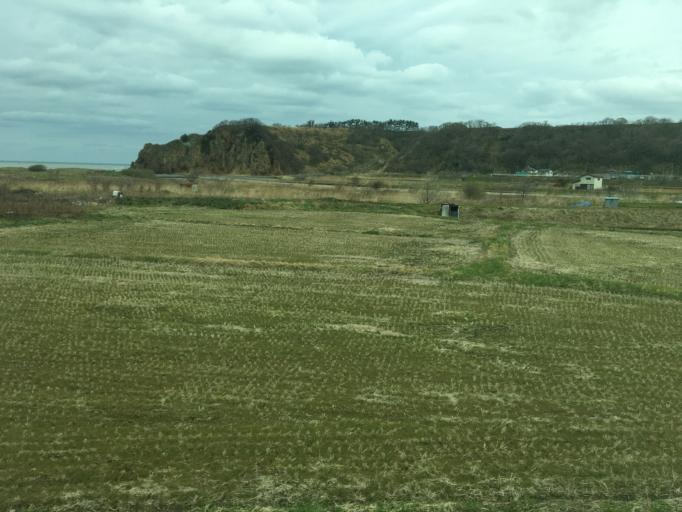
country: JP
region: Aomori
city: Shimokizukuri
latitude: 40.6830
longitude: 139.9682
